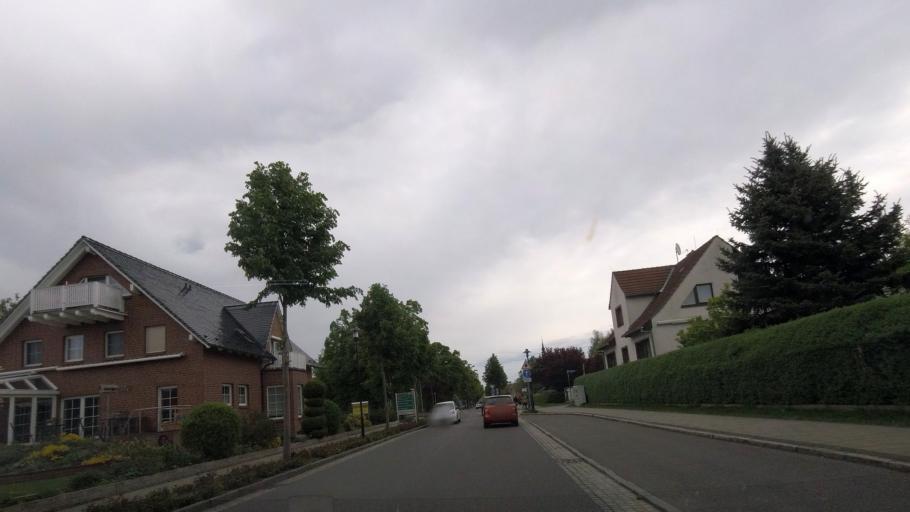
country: DE
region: Brandenburg
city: Lubbenau
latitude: 51.8651
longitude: 13.9645
